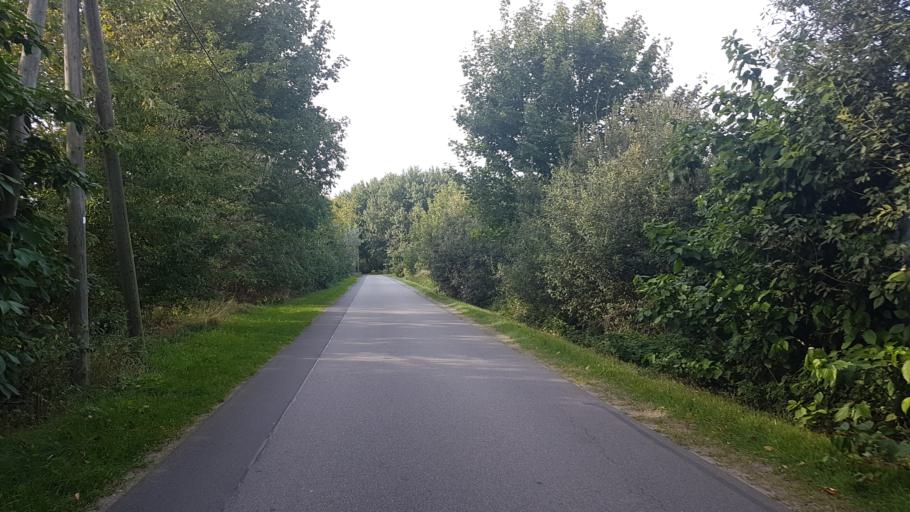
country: DE
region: Mecklenburg-Vorpommern
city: Hiddensee
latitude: 54.4592
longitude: 13.1376
